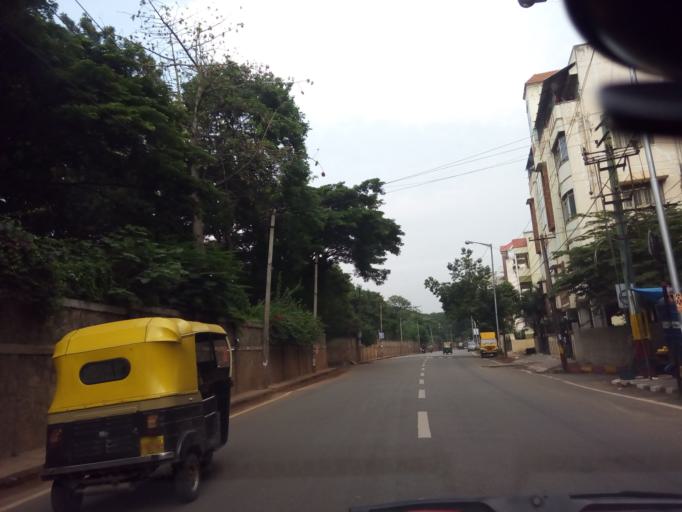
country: IN
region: Karnataka
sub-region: Bangalore Urban
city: Bangalore
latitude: 13.0248
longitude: 77.5625
